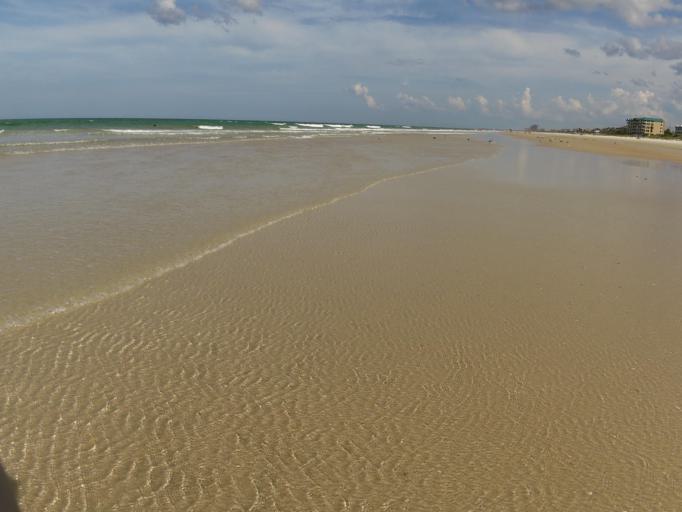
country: US
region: Florida
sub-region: Volusia County
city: Ponce Inlet
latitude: 29.0941
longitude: -80.9315
